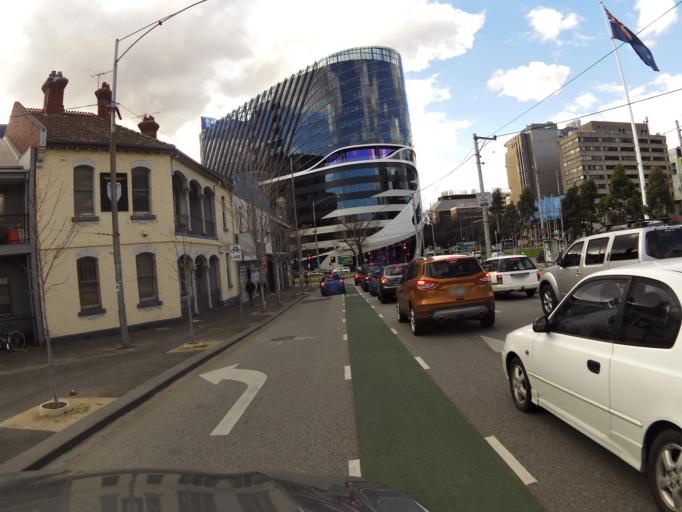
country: AU
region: Victoria
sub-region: Melbourne
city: North Melbourne
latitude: -37.8018
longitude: 144.9565
